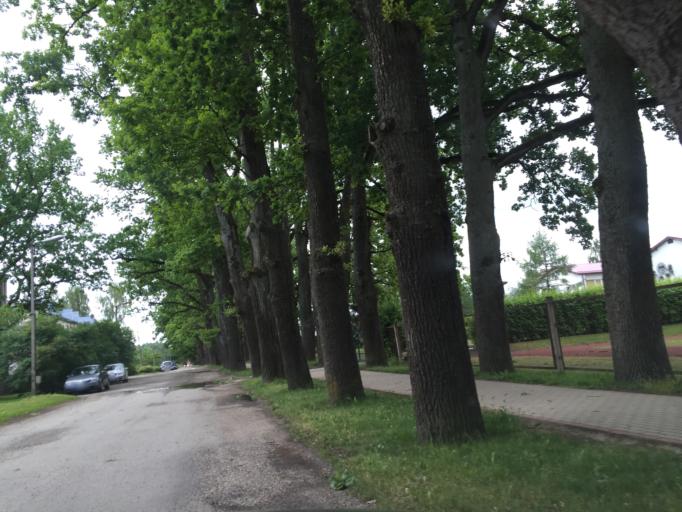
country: LV
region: Lecava
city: Iecava
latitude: 56.5927
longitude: 24.2021
